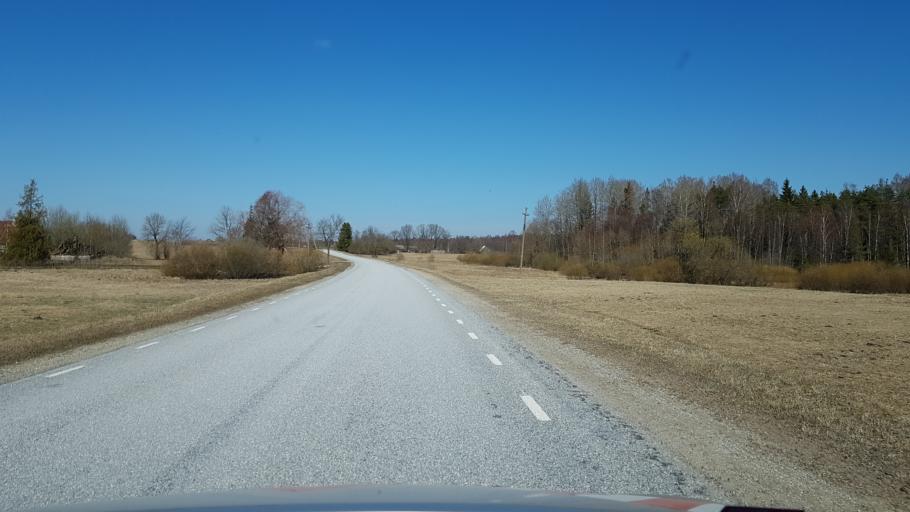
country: EE
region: Jaervamaa
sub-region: Koeru vald
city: Koeru
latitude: 59.0395
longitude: 26.0918
